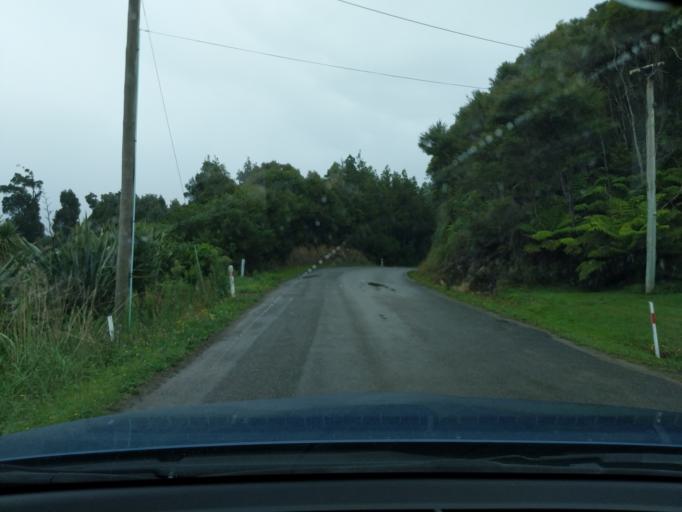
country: NZ
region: Tasman
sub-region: Tasman District
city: Takaka
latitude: -40.6419
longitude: 172.4834
